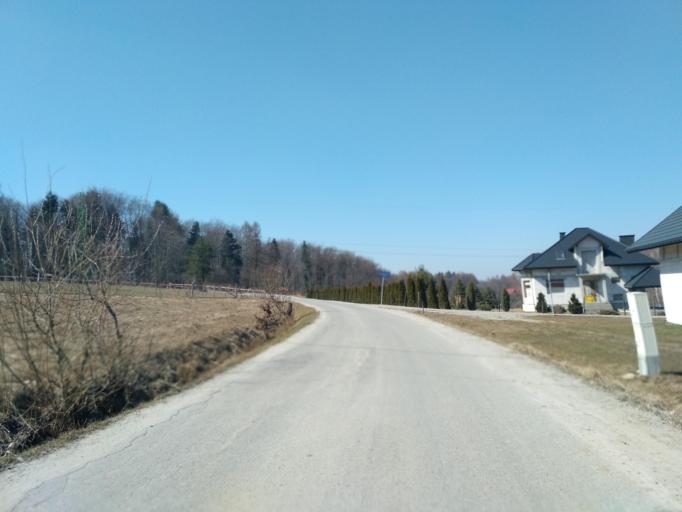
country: PL
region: Subcarpathian Voivodeship
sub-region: Powiat strzyzowski
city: Czudec
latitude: 49.9697
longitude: 21.8427
